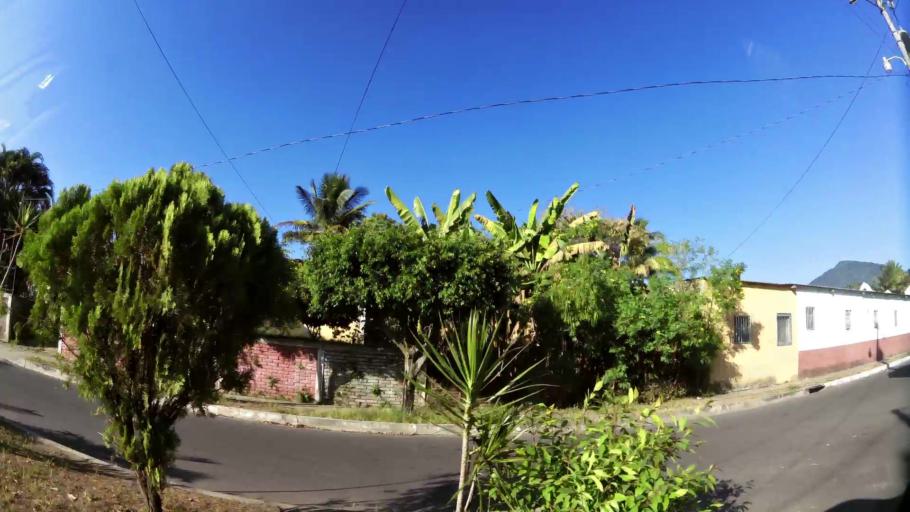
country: SV
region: La Libertad
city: Santa Tecla
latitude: 13.7352
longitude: -89.3561
